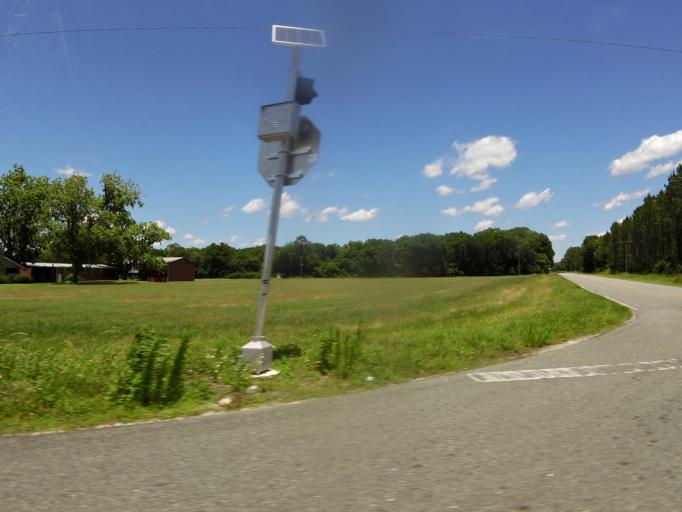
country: US
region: Florida
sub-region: Bradford County
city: Starke
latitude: 30.0439
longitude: -82.1403
